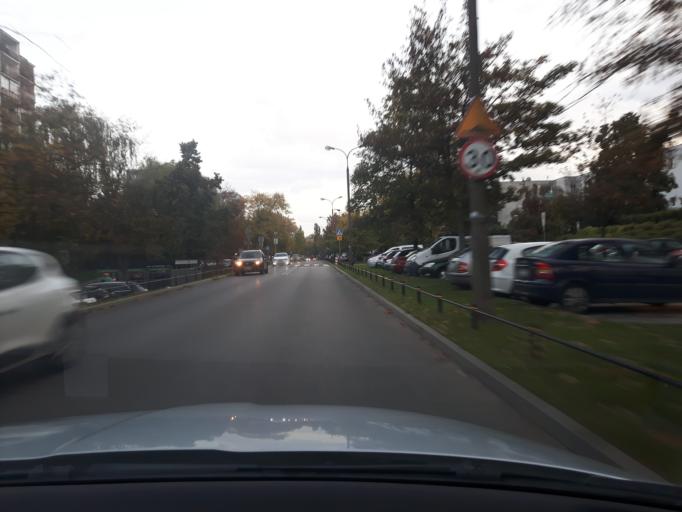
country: PL
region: Masovian Voivodeship
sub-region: Warszawa
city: Ursynow
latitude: 52.1415
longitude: 21.0509
